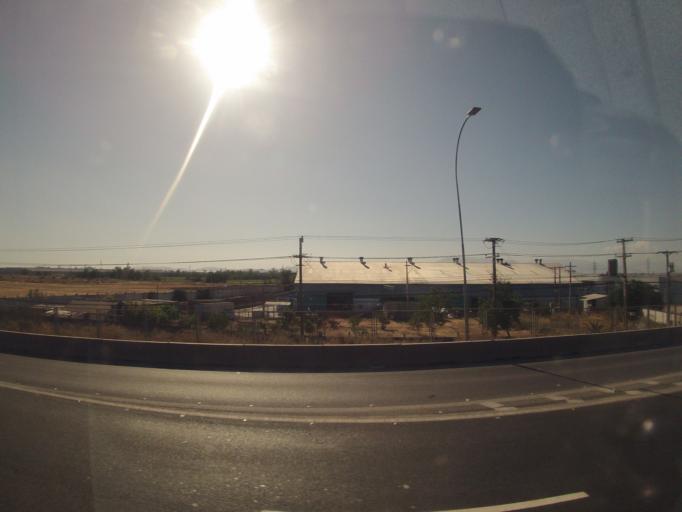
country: CL
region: Santiago Metropolitan
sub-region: Provincia de Maipo
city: San Bernardo
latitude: -33.5333
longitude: -70.7067
